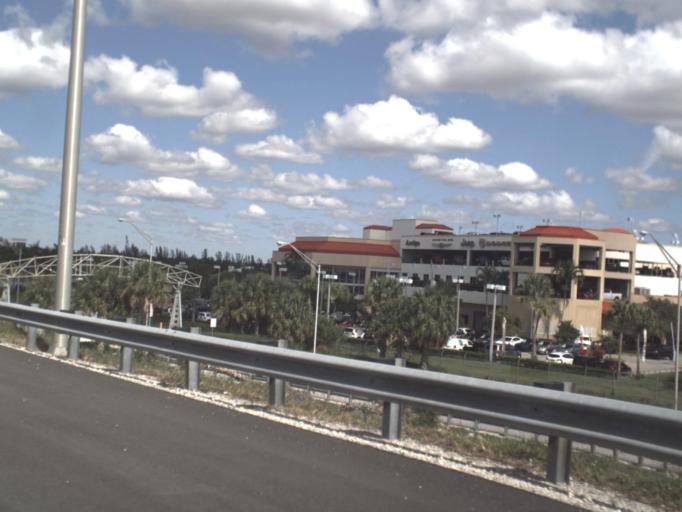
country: US
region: Florida
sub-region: Broward County
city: Tamarac
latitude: 26.1952
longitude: -80.2946
